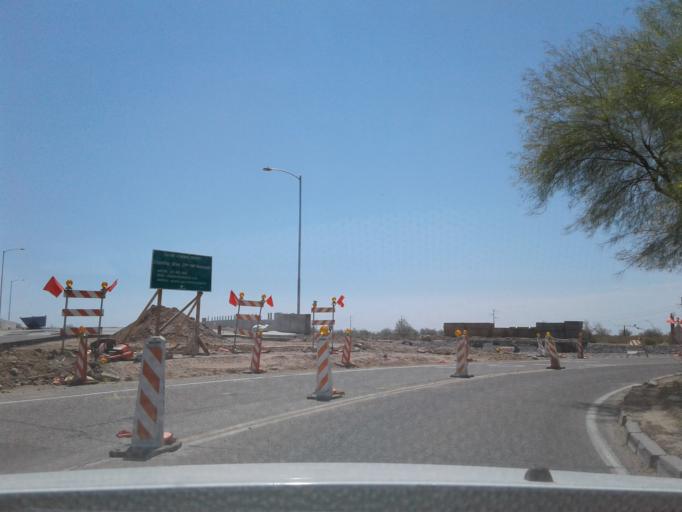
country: US
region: Arizona
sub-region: Maricopa County
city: Laveen
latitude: 33.2955
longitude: -112.1175
